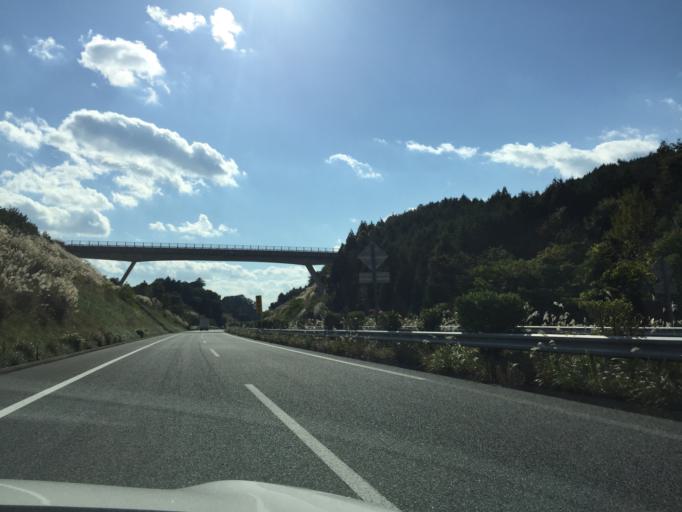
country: JP
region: Fukushima
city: Iwaki
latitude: 37.1917
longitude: 140.9860
